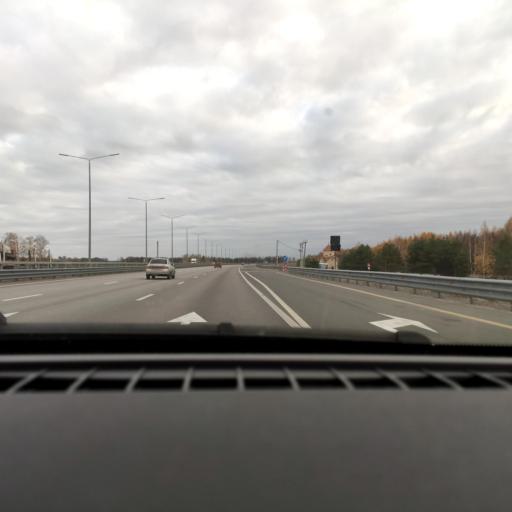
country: RU
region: Voronezj
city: Somovo
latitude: 51.7877
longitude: 39.2817
